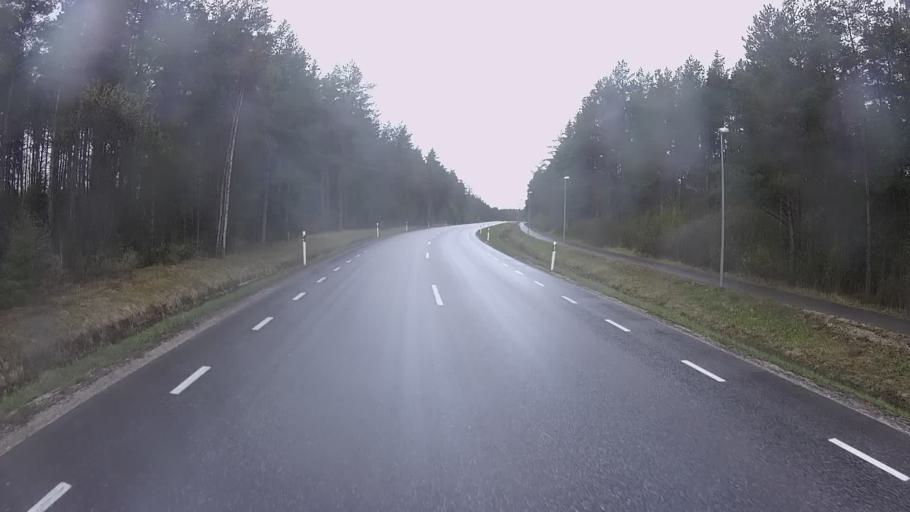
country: EE
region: Hiiumaa
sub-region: Kaerdla linn
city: Kardla
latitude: 58.9799
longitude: 22.5085
